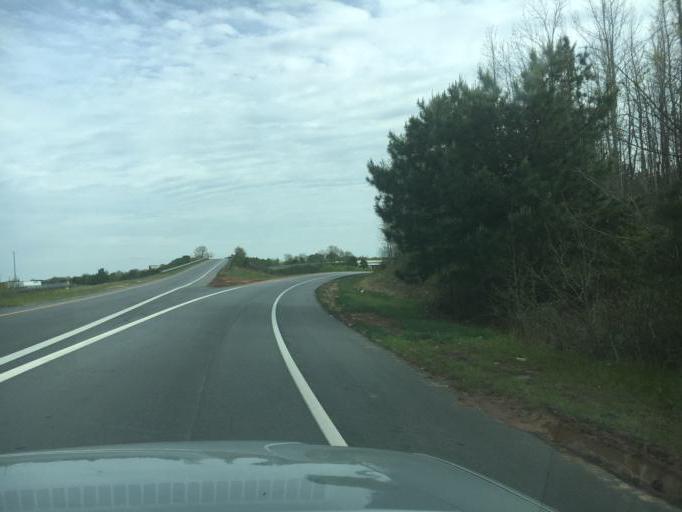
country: US
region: South Carolina
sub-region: Greenville County
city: Greer
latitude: 34.8897
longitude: -82.1934
